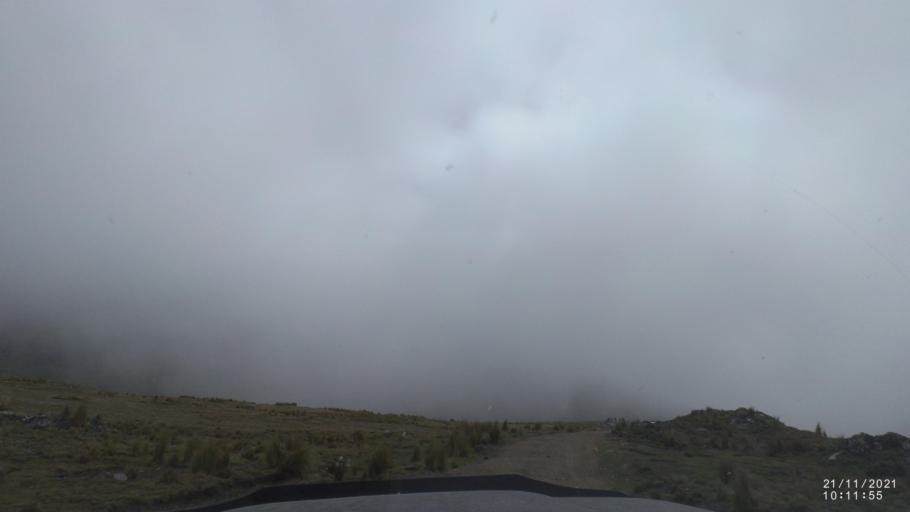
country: BO
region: Cochabamba
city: Cochabamba
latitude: -16.9924
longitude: -66.2688
